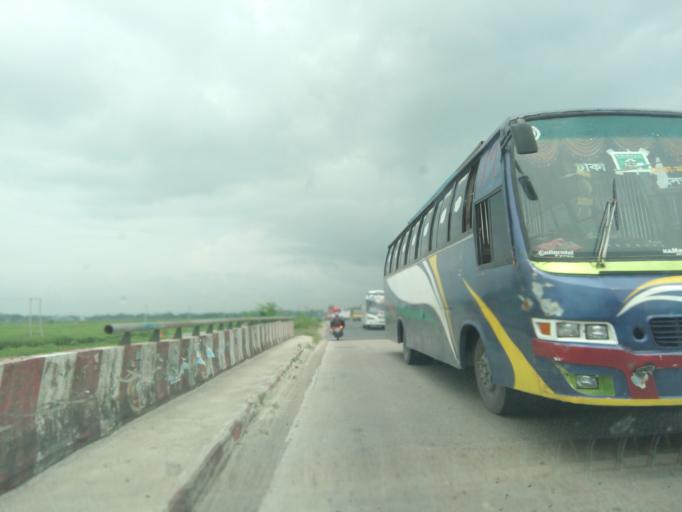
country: BD
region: Dhaka
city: Char Bhadrasan
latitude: 23.3701
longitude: 90.0498
